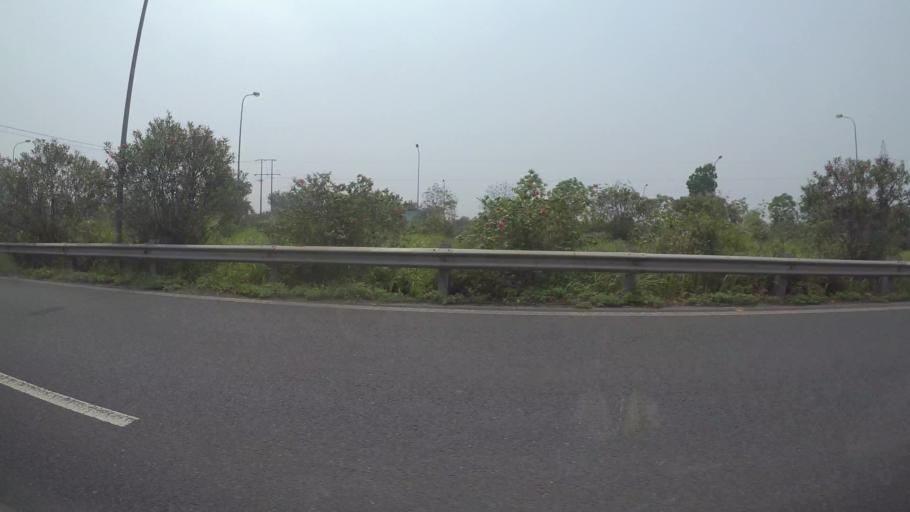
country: VN
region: Ha Noi
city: Quoc Oai
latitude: 21.0026
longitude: 105.6293
